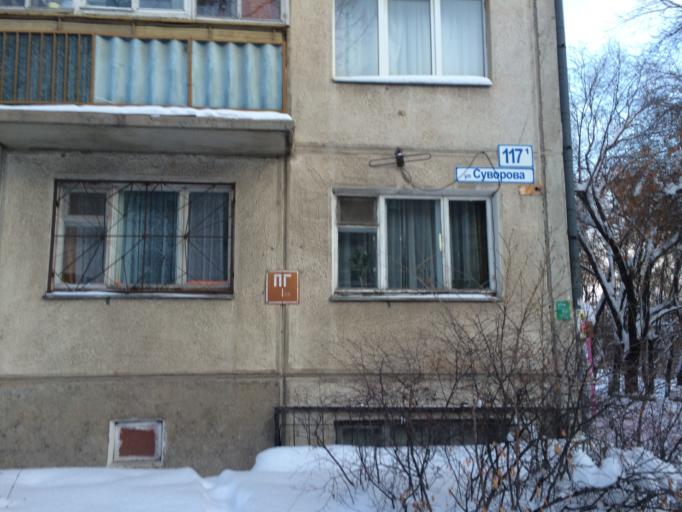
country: RU
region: Chelyabinsk
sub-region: Gorod Magnitogorsk
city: Magnitogorsk
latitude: 53.4021
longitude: 58.9717
